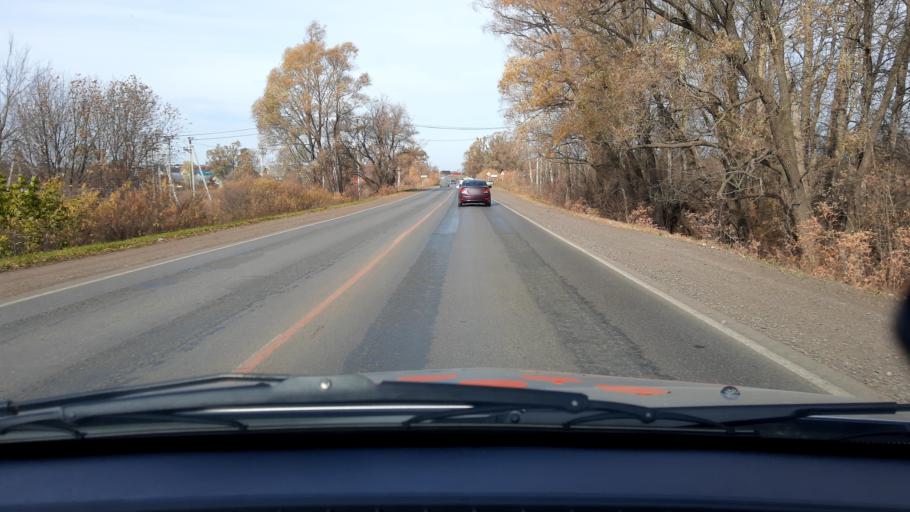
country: RU
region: Bashkortostan
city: Avdon
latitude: 54.7319
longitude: 55.8044
